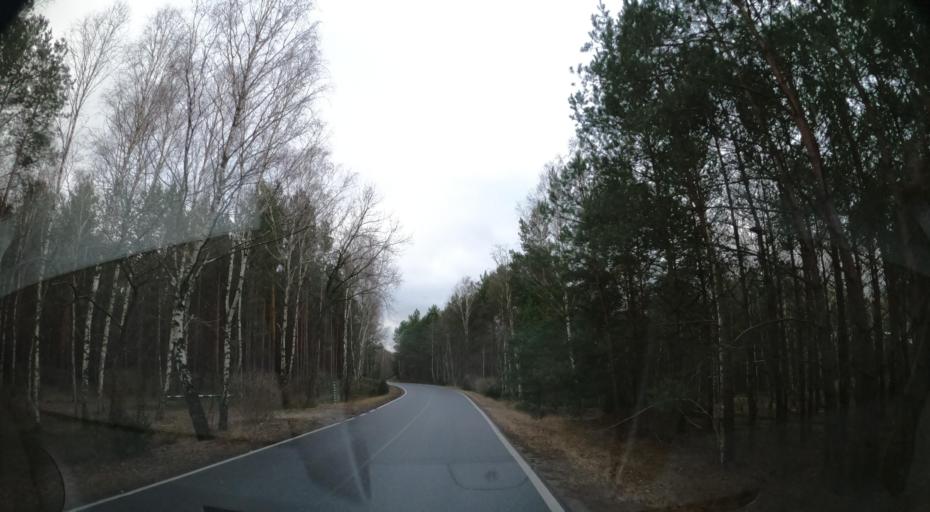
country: PL
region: Kujawsko-Pomorskie
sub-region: Powiat bydgoski
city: Solec Kujawski
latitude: 53.0576
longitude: 18.2281
